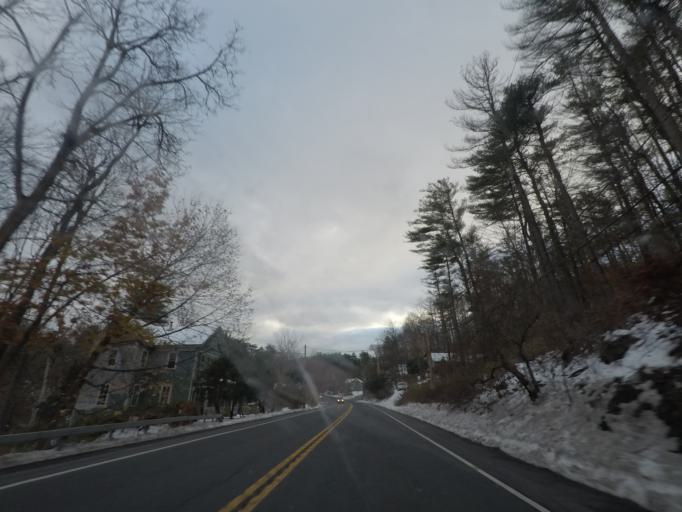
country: US
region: New York
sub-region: Ulster County
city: Hurley
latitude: 41.8870
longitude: -74.0442
